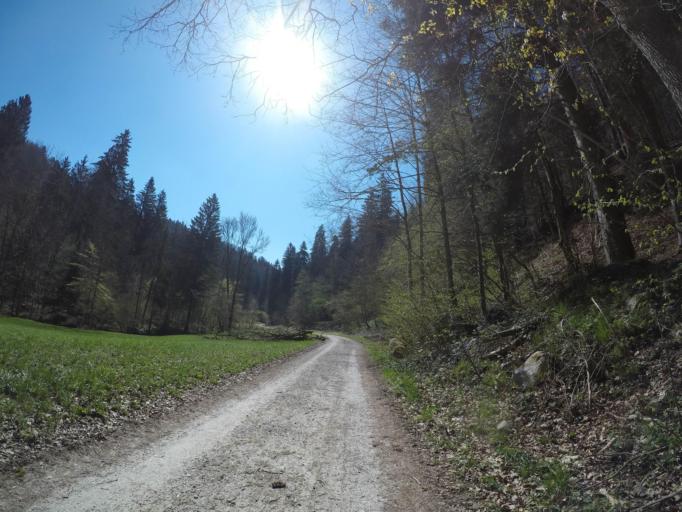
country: DE
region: Baden-Wuerttemberg
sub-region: Tuebingen Region
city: Horgenzell
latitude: 47.8074
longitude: 9.4620
